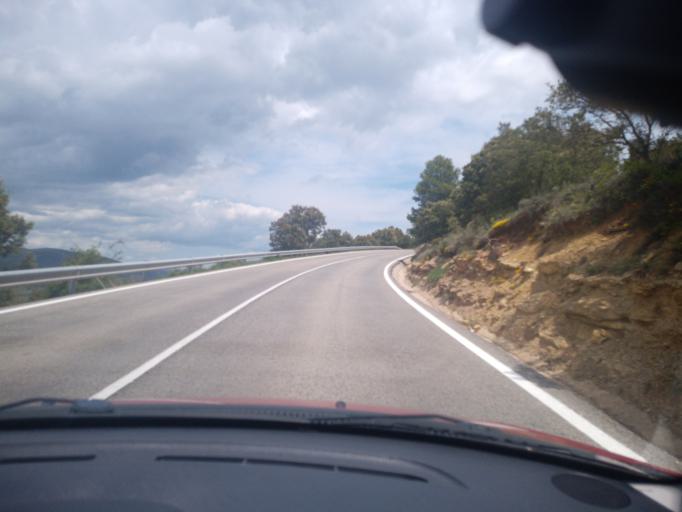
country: ES
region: Valencia
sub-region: Provincia de Castello
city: Ares del Maestre
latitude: 40.4582
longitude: -0.1586
